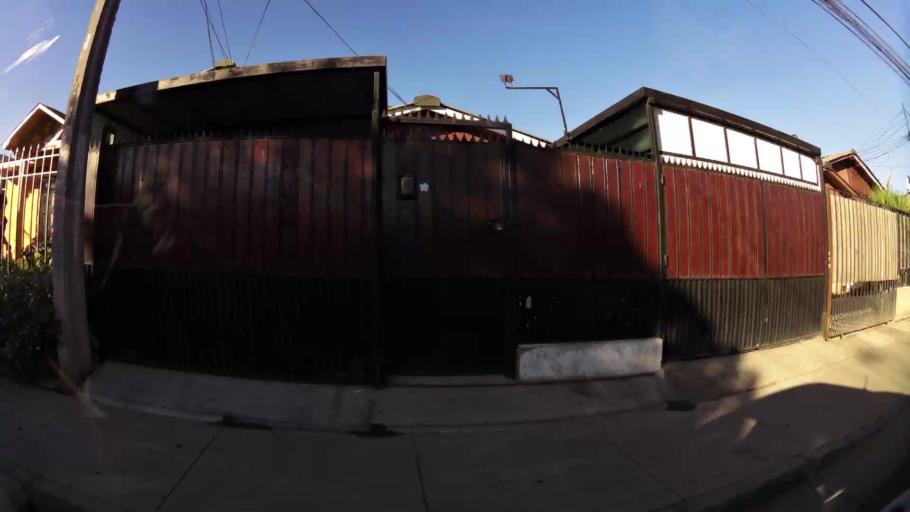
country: CL
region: O'Higgins
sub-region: Provincia de Cachapoal
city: Rancagua
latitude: -34.1768
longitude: -70.7627
